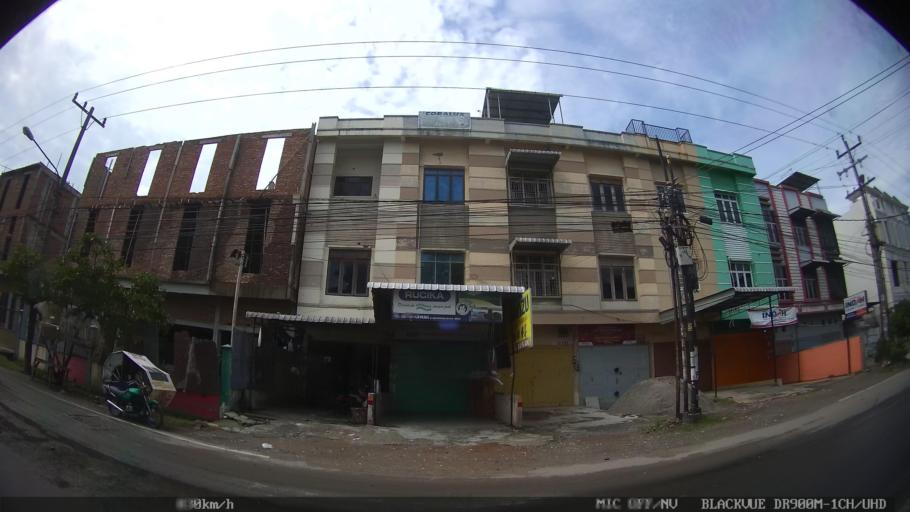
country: ID
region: North Sumatra
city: Medan
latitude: 3.6221
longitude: 98.7022
